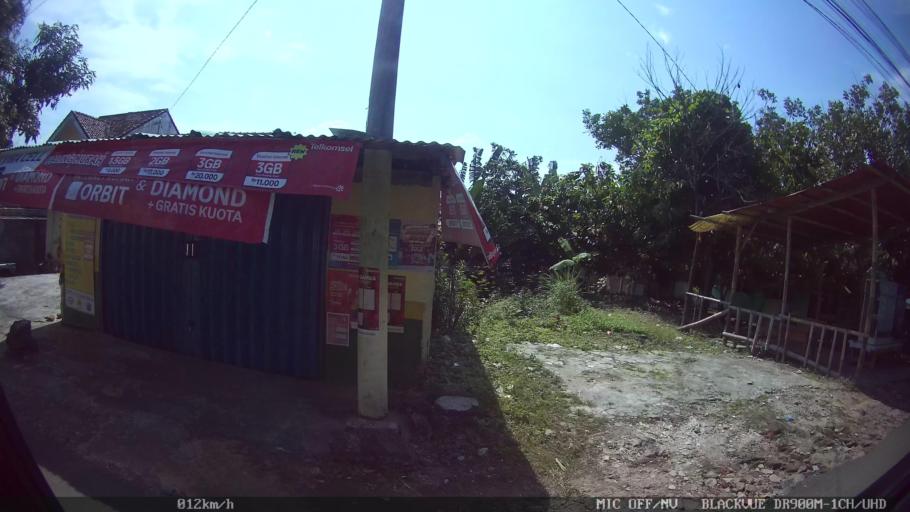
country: ID
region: Lampung
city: Kedaton
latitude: -5.4006
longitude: 105.2502
